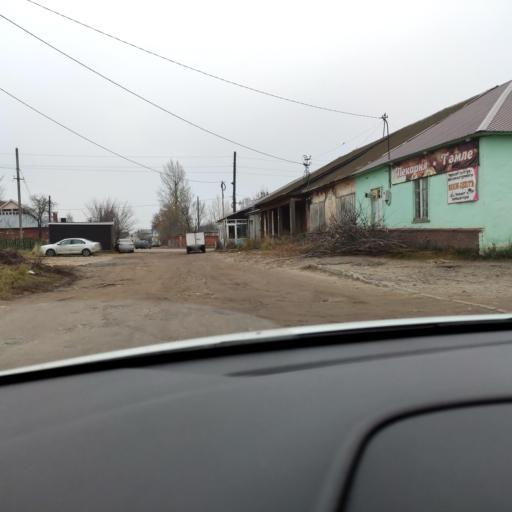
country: RU
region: Tatarstan
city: Vysokaya Gora
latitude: 55.8487
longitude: 49.2195
